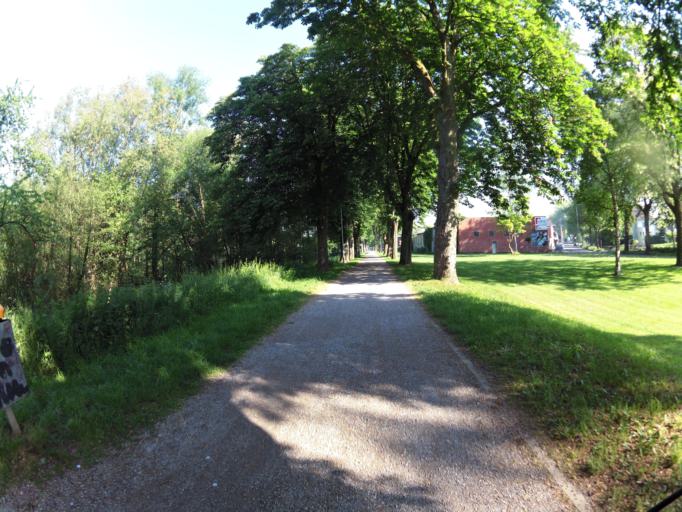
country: DE
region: North Rhine-Westphalia
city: Julich
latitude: 50.9221
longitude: 6.3518
